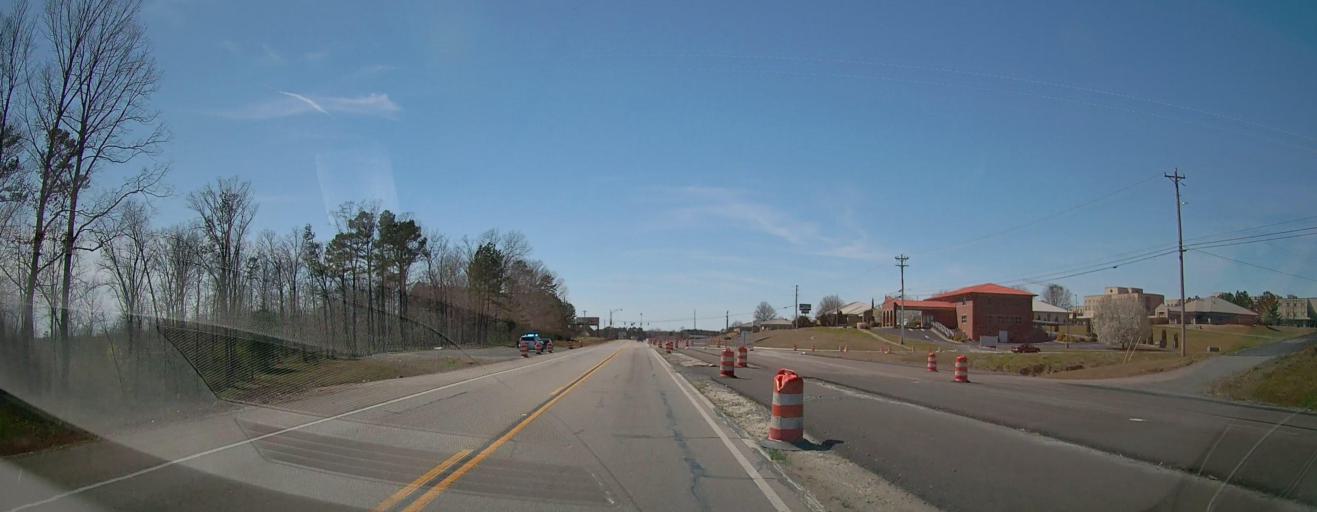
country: US
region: Alabama
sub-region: Cullman County
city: Cullman
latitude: 34.1988
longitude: -86.8004
